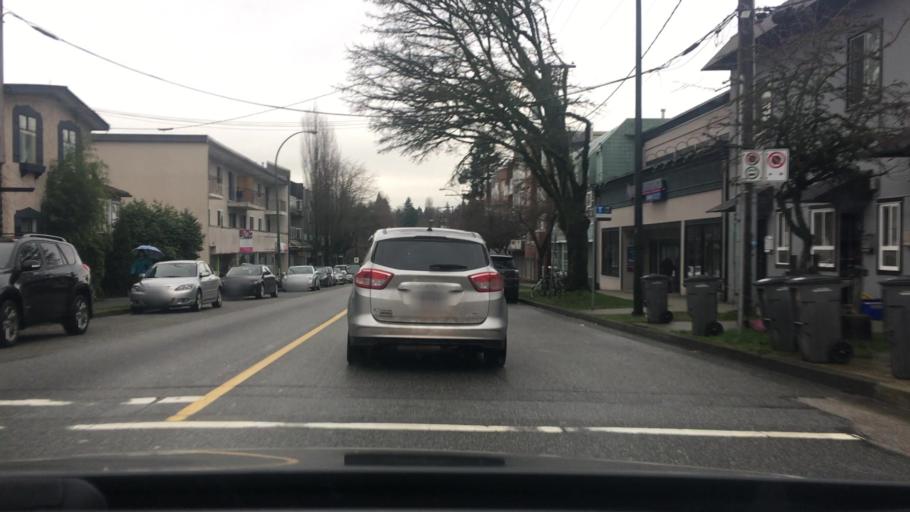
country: CA
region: British Columbia
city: Vancouver
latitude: 49.2570
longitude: -123.1201
